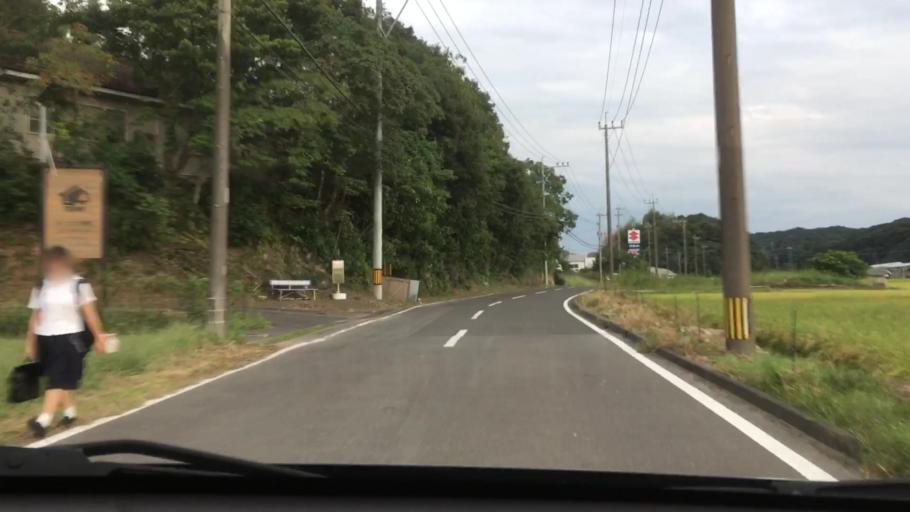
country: JP
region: Nagasaki
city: Sasebo
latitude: 32.9955
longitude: 129.7696
